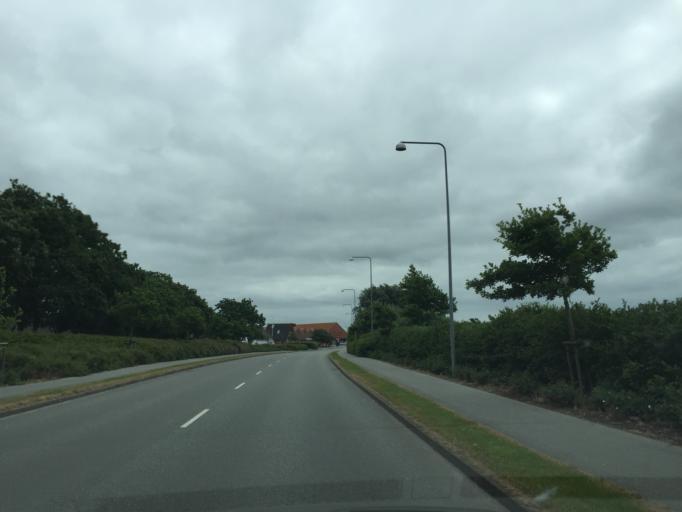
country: DK
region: South Denmark
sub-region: Tonder Kommune
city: Sherrebek
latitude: 55.1610
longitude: 8.7590
